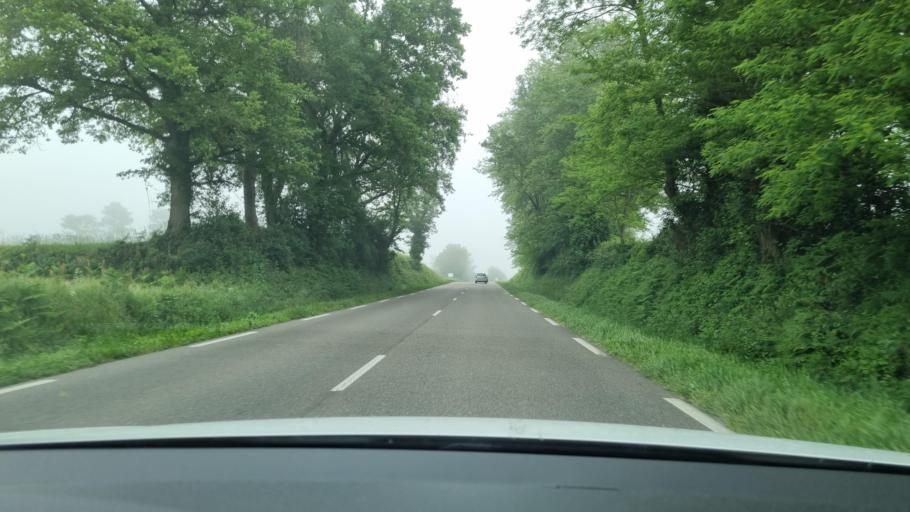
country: FR
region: Aquitaine
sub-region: Departement des Landes
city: Hagetmau
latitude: 43.6275
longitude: -0.6240
